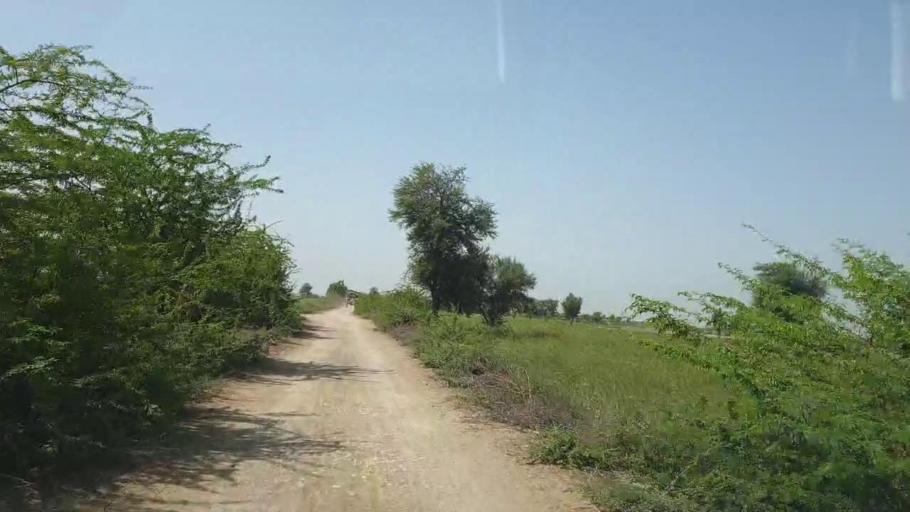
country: PK
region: Sindh
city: Naukot
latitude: 24.9077
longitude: 69.4842
